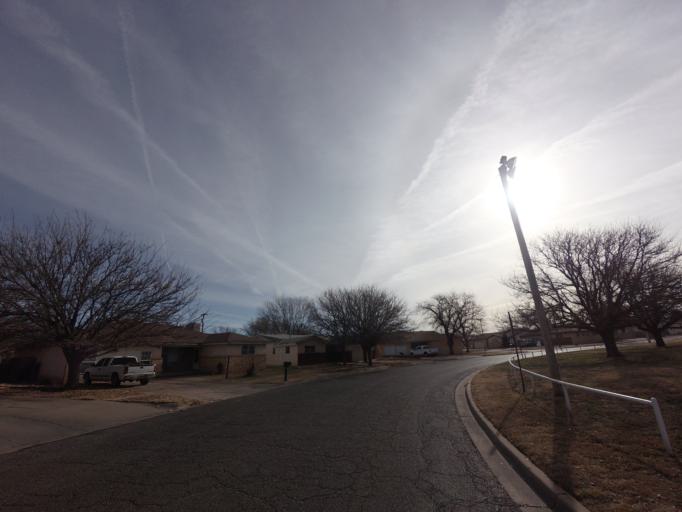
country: US
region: New Mexico
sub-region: Curry County
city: Clovis
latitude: 34.4135
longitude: -103.2178
